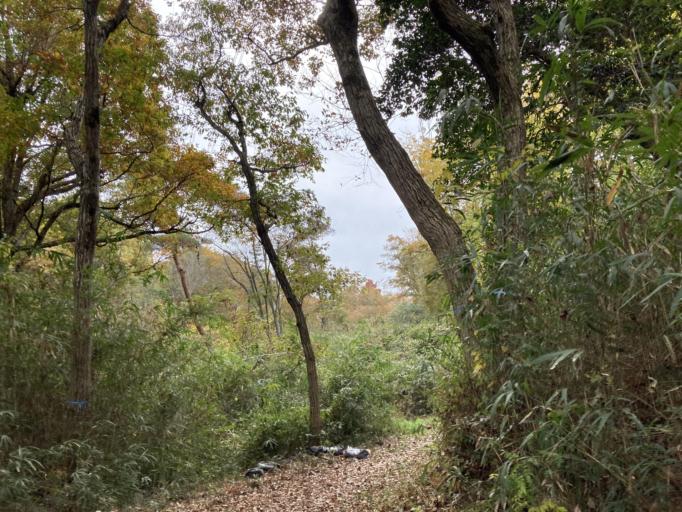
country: JP
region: Osaka
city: Hirakata
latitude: 34.7698
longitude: 135.7084
